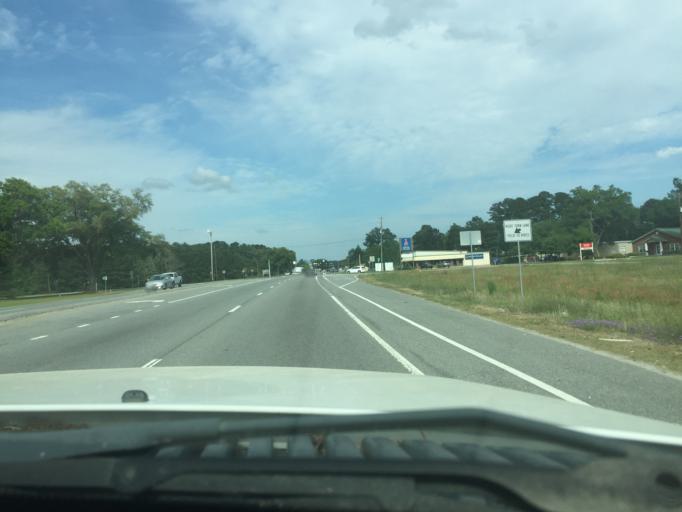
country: US
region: Georgia
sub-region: Chatham County
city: Georgetown
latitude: 31.9966
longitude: -81.2640
